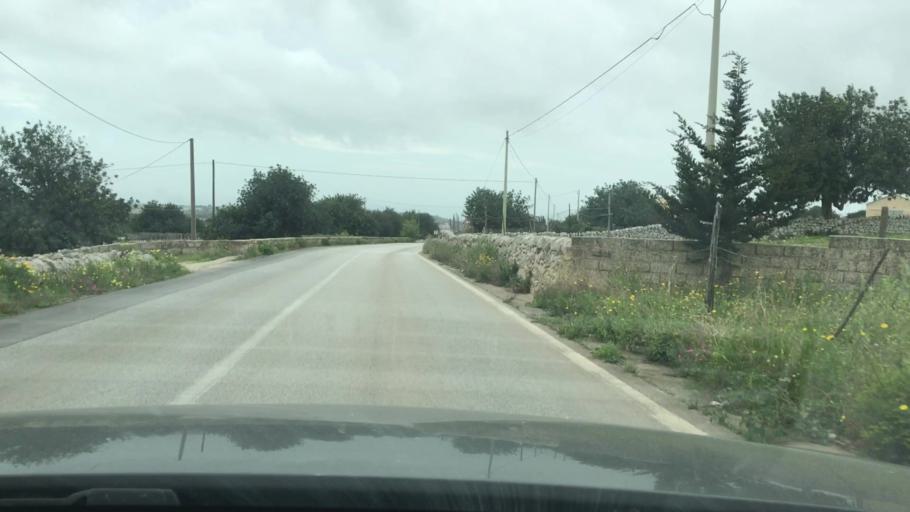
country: IT
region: Sicily
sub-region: Ragusa
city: Scicli
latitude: 36.8069
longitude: 14.7245
